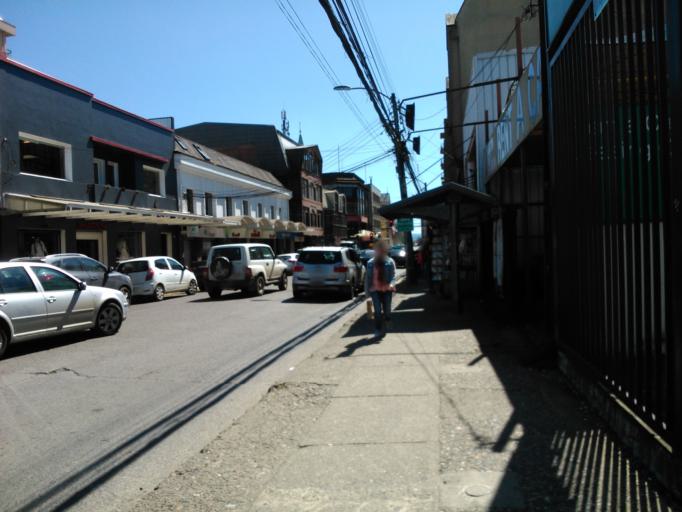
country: CL
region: Los Rios
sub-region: Provincia de Valdivia
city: Valdivia
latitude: -39.8159
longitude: -73.2467
